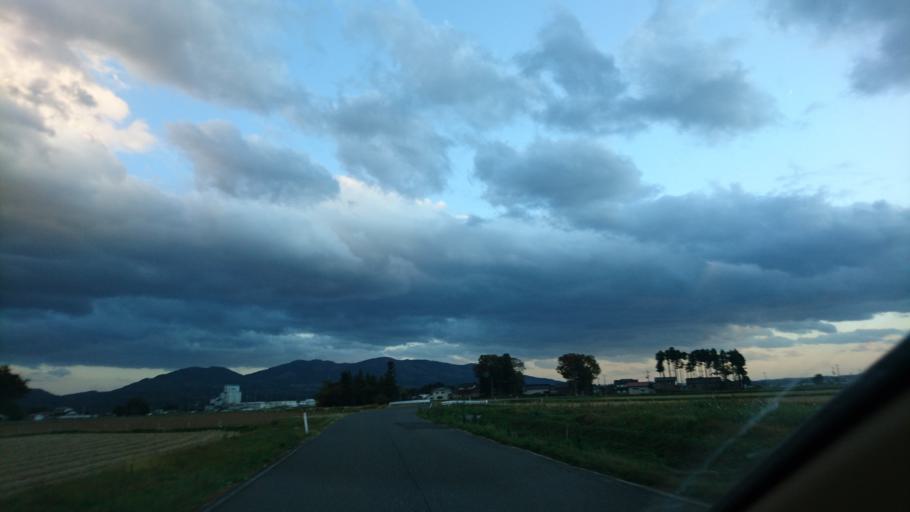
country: JP
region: Iwate
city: Mizusawa
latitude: 39.0753
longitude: 141.1412
